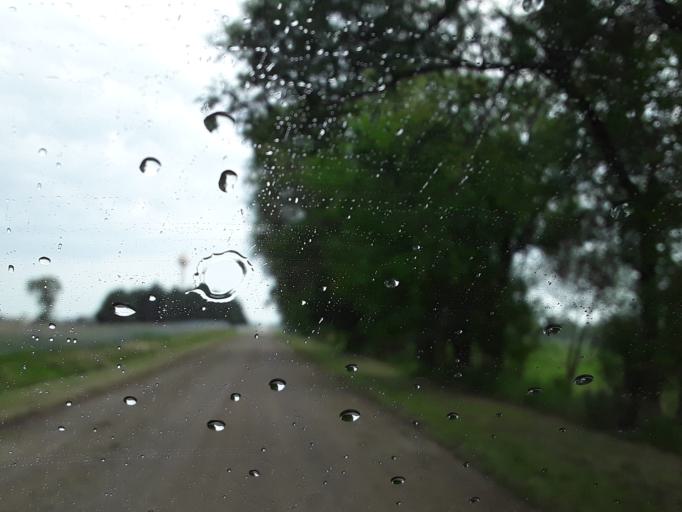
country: US
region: Nebraska
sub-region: Saunders County
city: Yutan
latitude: 41.1902
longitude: -96.4449
